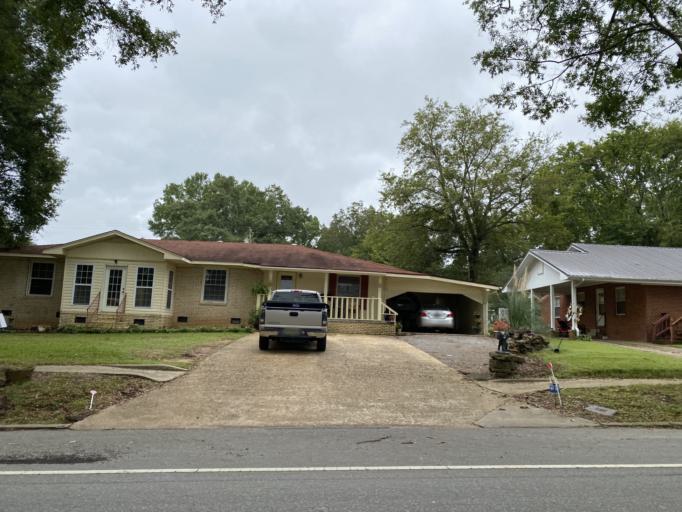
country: US
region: Alabama
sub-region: Franklin County
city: Red Bay
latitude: 34.4427
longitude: -88.1511
